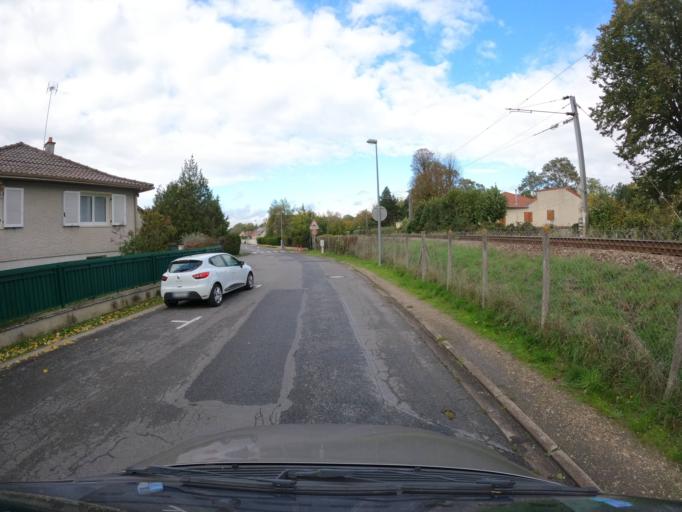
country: FR
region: Ile-de-France
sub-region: Departement de Seine-et-Marne
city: Saint-Germain-sur-Morin
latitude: 48.8840
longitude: 2.8530
